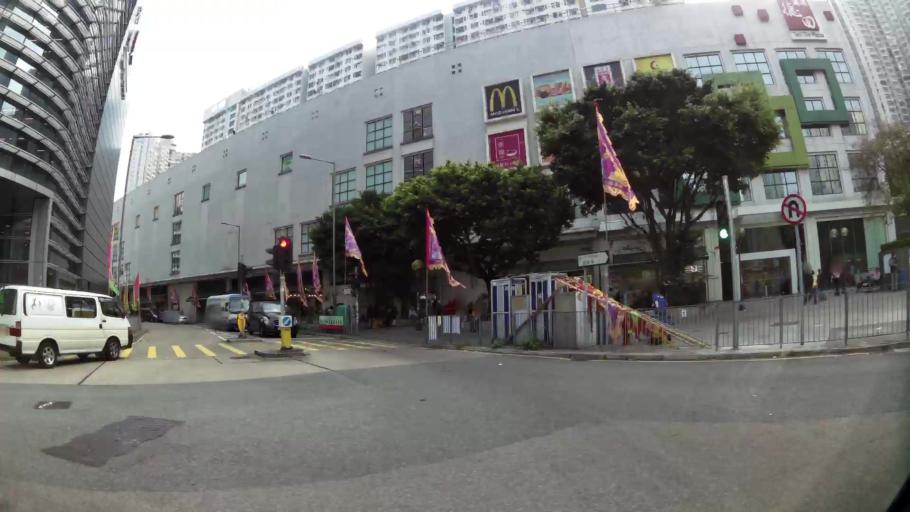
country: HK
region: Kowloon City
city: Kowloon
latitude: 22.3099
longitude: 114.2378
